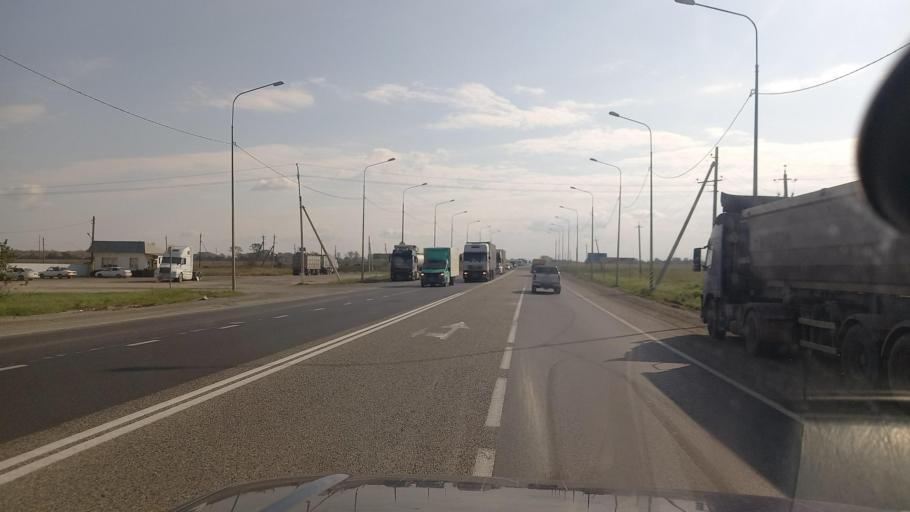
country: RU
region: Krasnodarskiy
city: Novoukrainskiy
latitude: 44.8939
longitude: 38.0632
